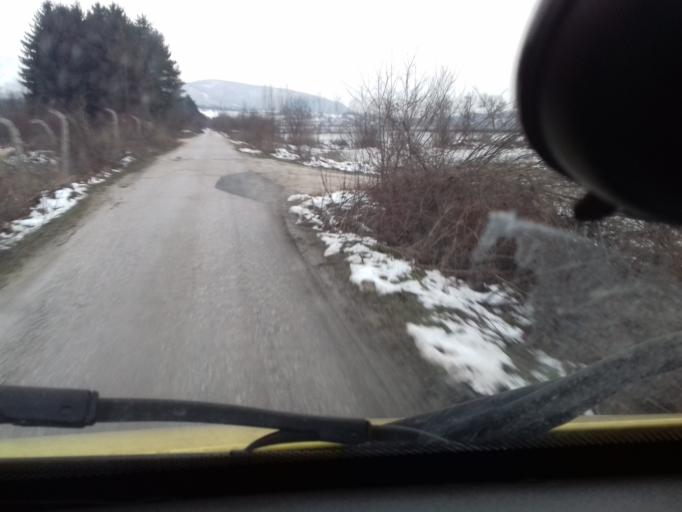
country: BA
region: Federation of Bosnia and Herzegovina
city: Vitez
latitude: 44.1583
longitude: 17.7778
